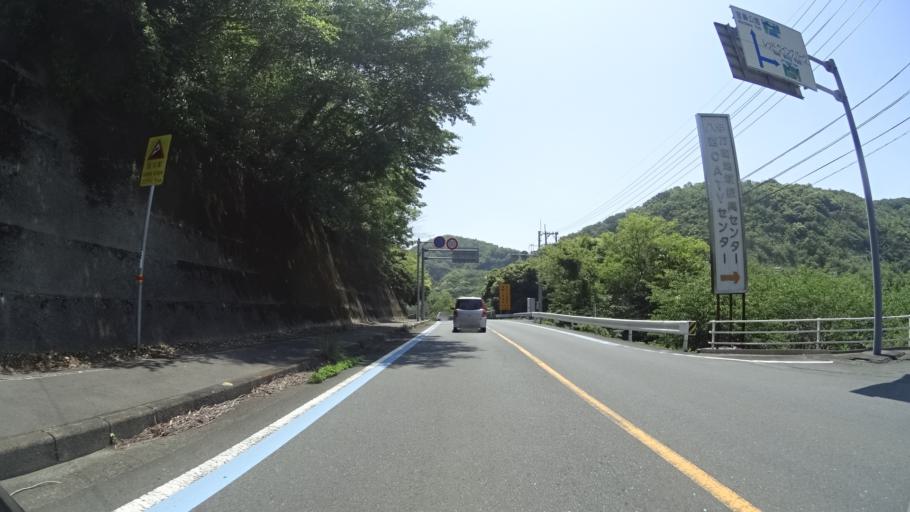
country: JP
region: Ehime
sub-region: Nishiuwa-gun
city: Ikata-cho
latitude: 33.4817
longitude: 132.3265
